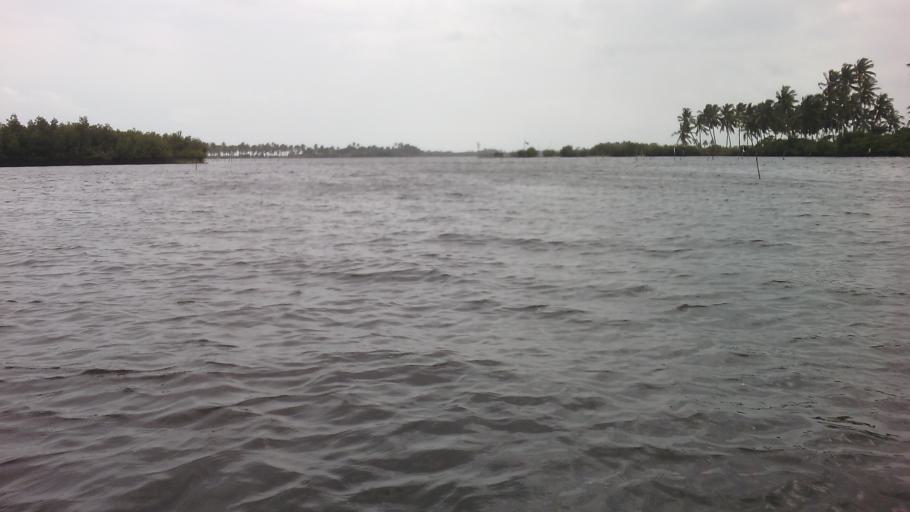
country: BJ
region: Atlantique
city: Ouidah
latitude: 6.3105
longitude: 1.9948
